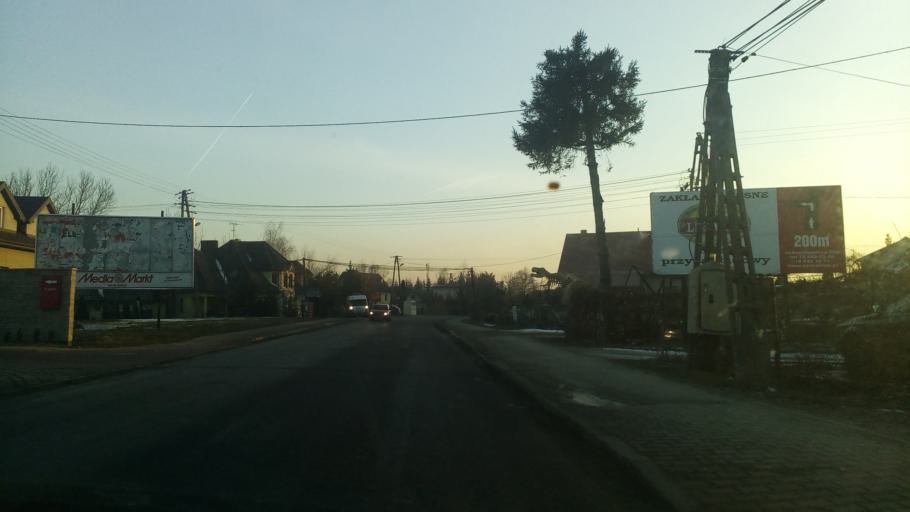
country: PL
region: Lesser Poland Voivodeship
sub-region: Powiat nowosadecki
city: Chelmiec
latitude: 49.6357
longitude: 20.6668
